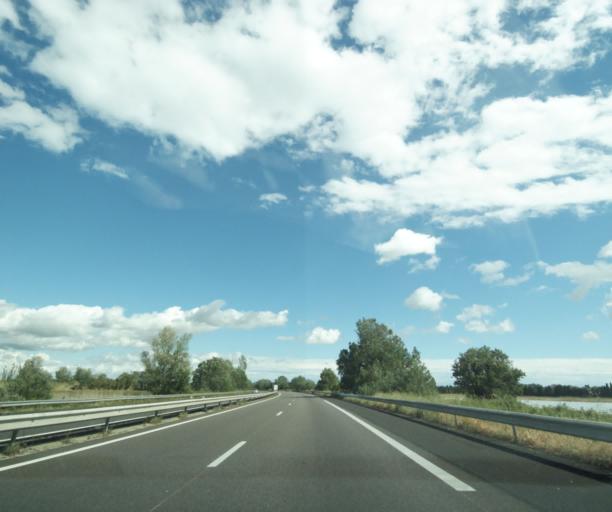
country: FR
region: Languedoc-Roussillon
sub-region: Departement du Gard
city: Bellegarde
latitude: 43.7133
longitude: 4.5138
